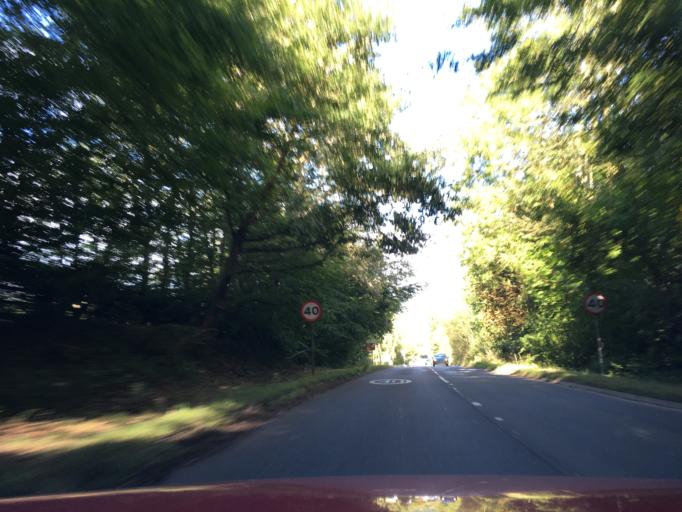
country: GB
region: England
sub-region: Devon
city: Newton Poppleford
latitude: 50.7004
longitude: -3.2716
